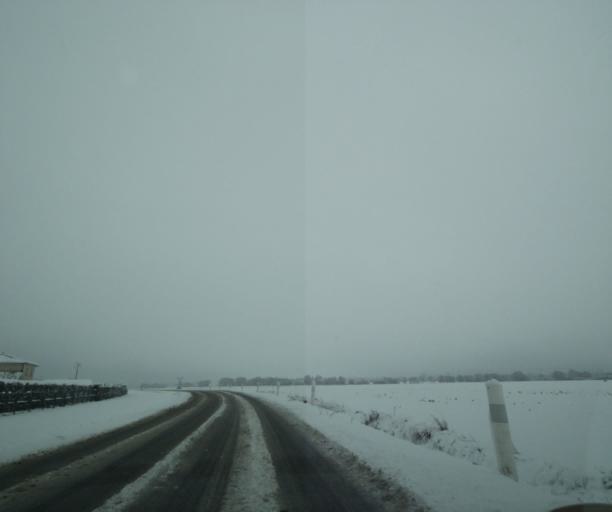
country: FR
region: Champagne-Ardenne
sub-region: Departement de la Haute-Marne
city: Saint-Dizier
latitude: 48.5787
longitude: 4.9062
